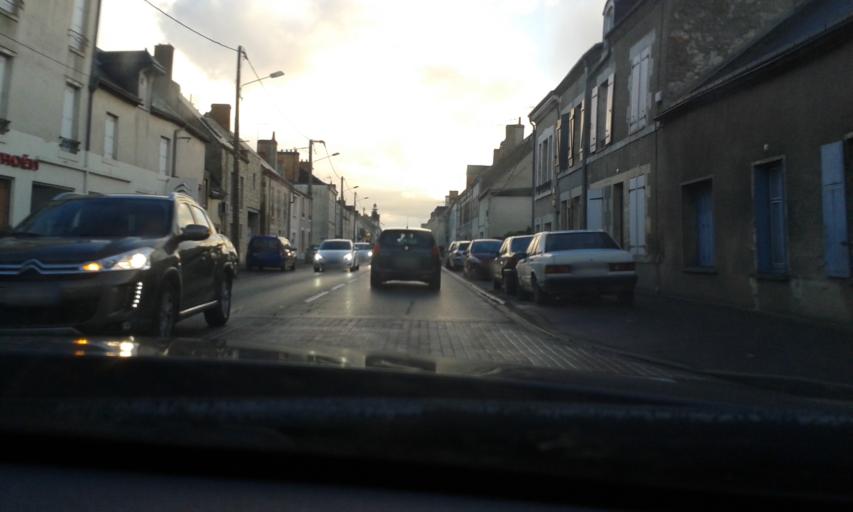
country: FR
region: Centre
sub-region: Departement du Loiret
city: Chevilly
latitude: 48.0291
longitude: 1.8743
